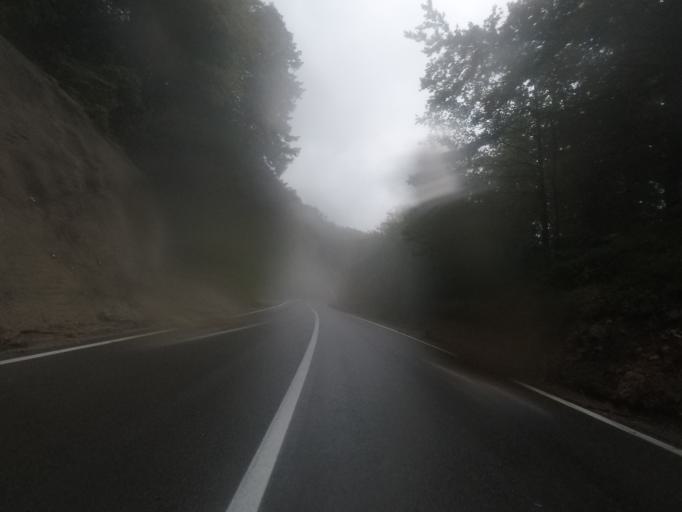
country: HR
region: Primorsko-Goranska
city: Hreljin
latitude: 45.3556
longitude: 14.6432
